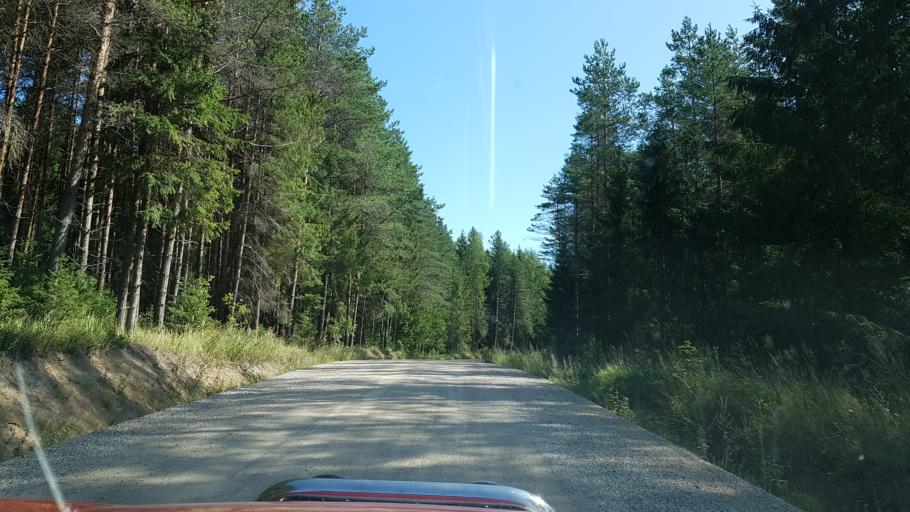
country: EE
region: Vorumaa
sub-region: Voru linn
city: Voru
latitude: 57.7359
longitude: 27.2343
